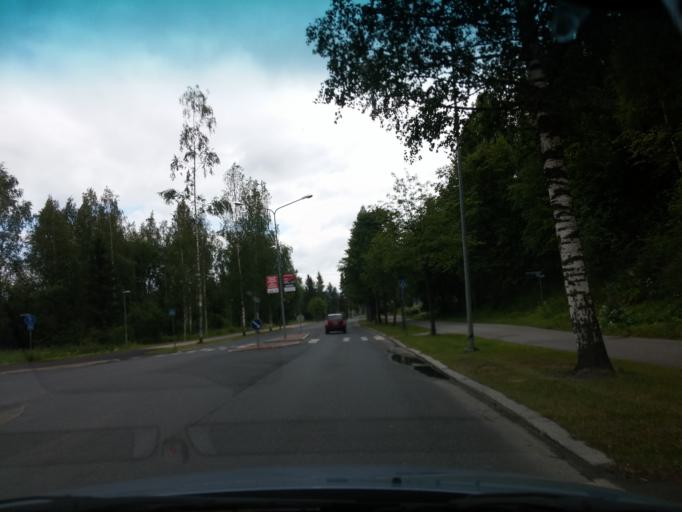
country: FI
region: Northern Savo
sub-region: Kuopio
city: Kuopio
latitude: 62.8345
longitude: 27.6143
